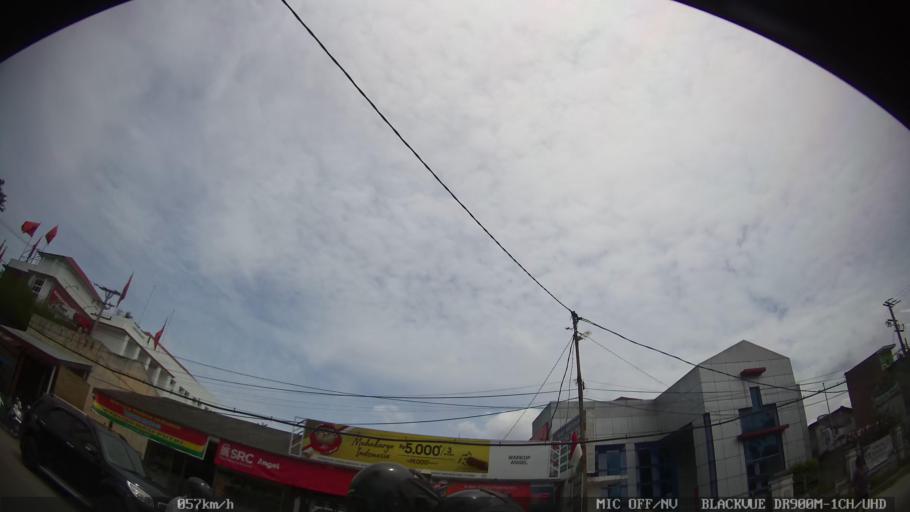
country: ID
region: North Sumatra
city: Sunggal
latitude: 3.5218
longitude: 98.6229
